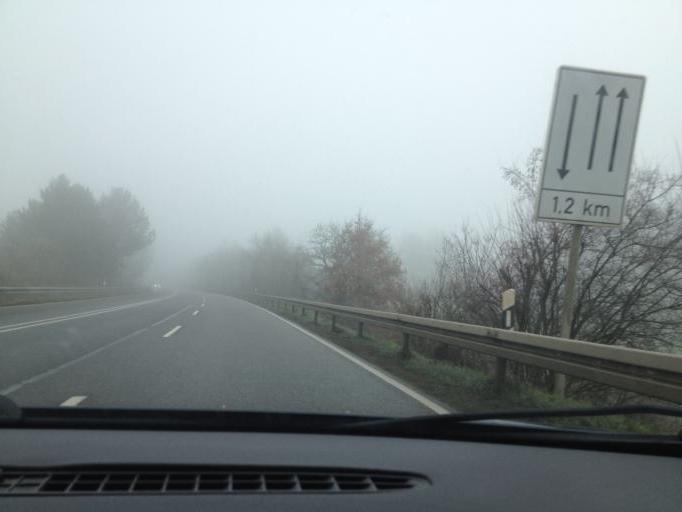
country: DE
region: Saarland
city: Sankt Wendel
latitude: 49.4875
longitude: 7.1505
